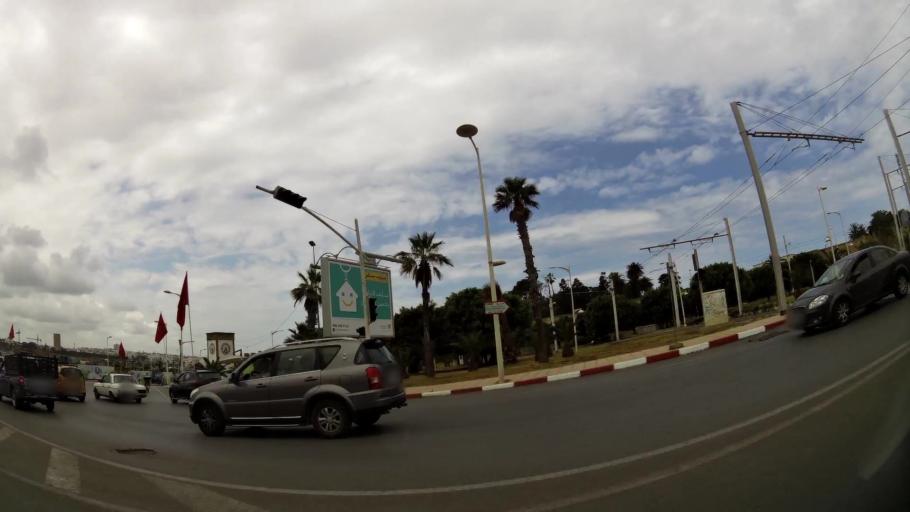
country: MA
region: Rabat-Sale-Zemmour-Zaer
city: Sale
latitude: 34.0352
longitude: -6.8176
